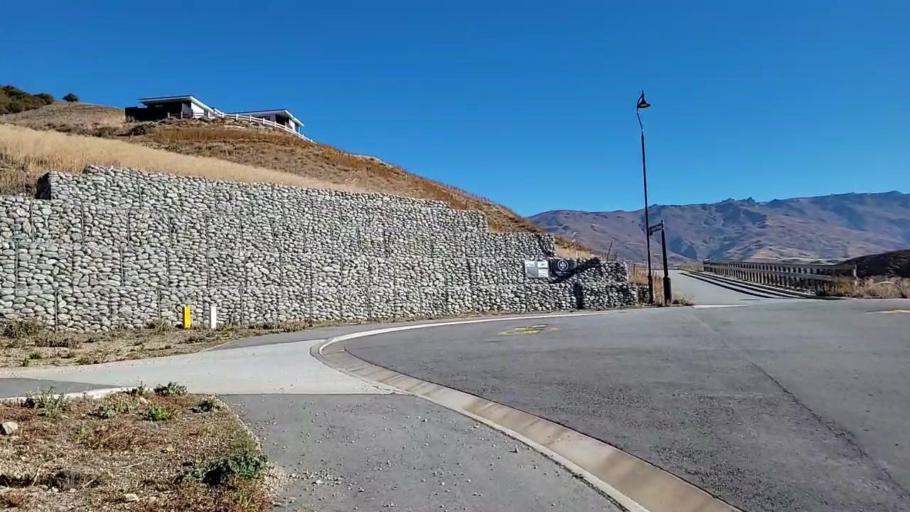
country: NZ
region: Otago
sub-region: Queenstown-Lakes District
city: Wanaka
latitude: -44.9982
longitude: 169.2060
